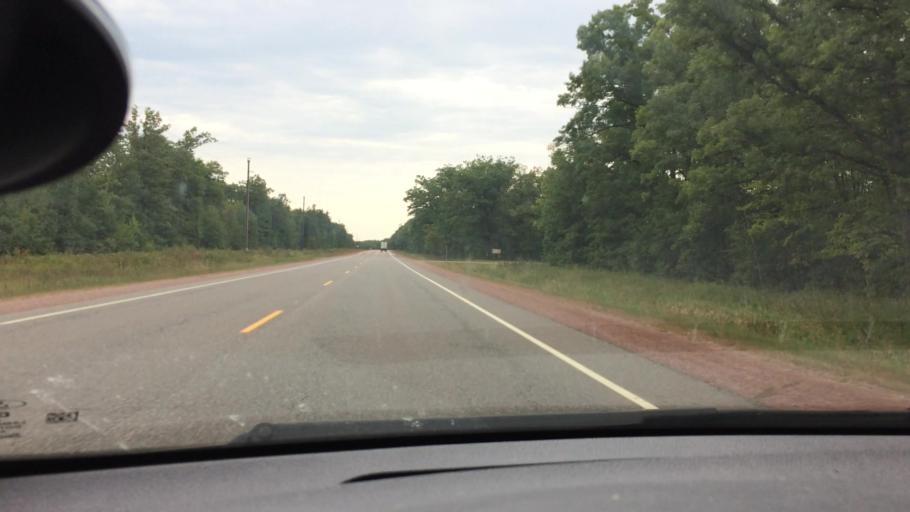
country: US
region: Wisconsin
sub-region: Clark County
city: Neillsville
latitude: 44.5774
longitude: -90.7365
